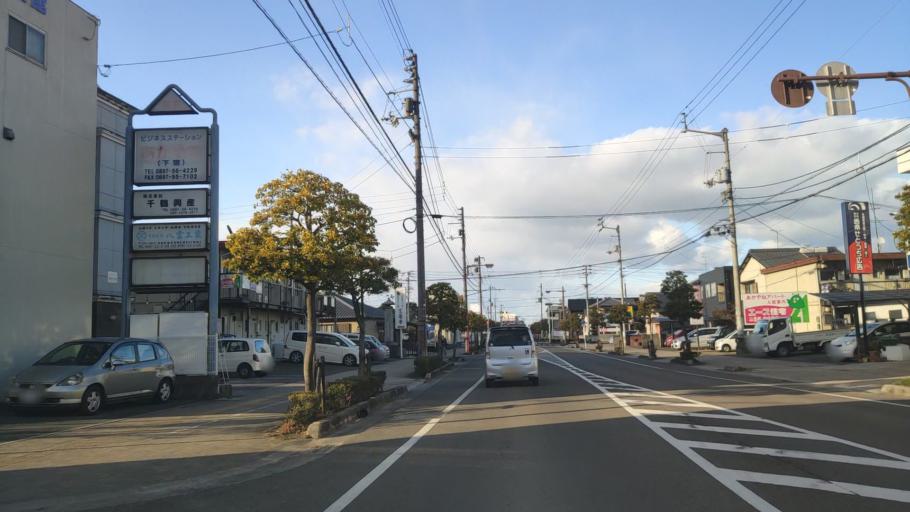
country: JP
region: Ehime
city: Saijo
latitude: 33.9201
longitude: 133.1849
